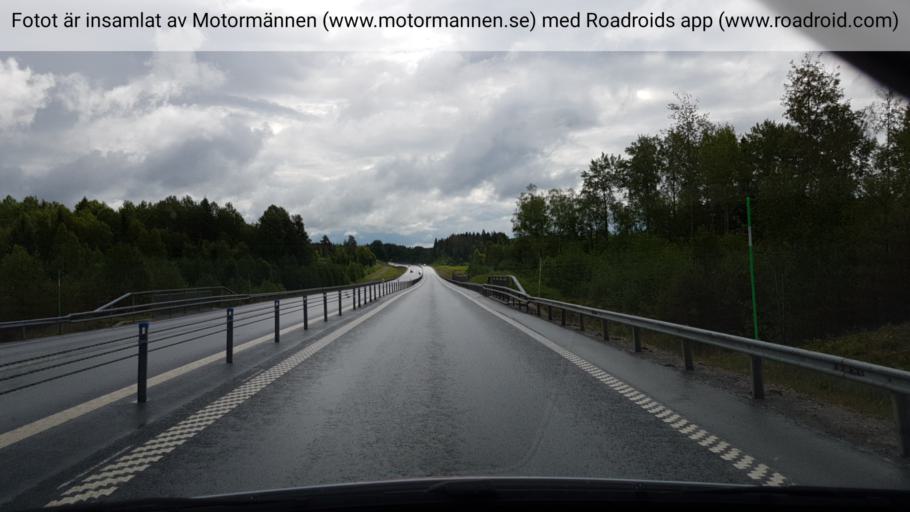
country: SE
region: Vaesterbotten
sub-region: Vannas Kommun
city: Vannasby
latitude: 63.8984
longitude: 19.9103
